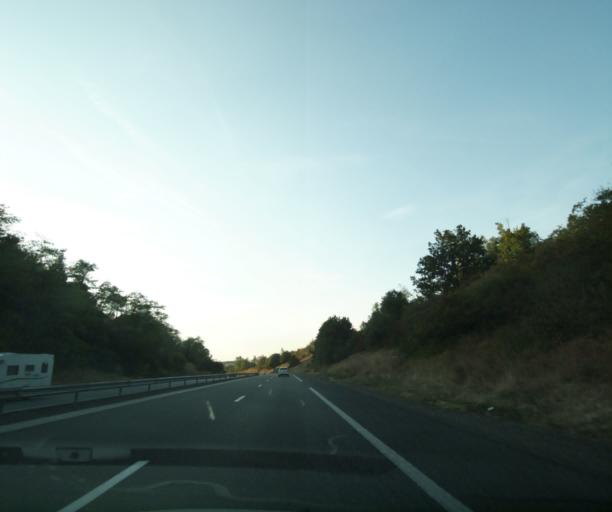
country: FR
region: Aquitaine
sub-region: Departement du Lot-et-Garonne
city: Boe
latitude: 44.1433
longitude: 0.6337
